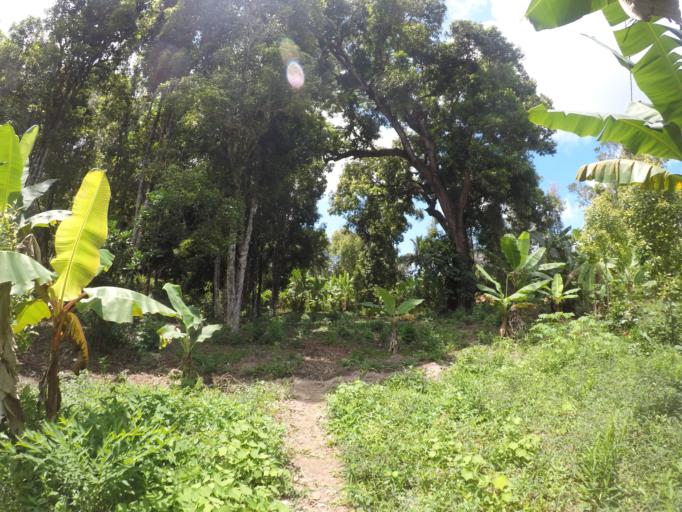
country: TZ
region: Pemba South
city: Mtambile
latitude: -5.3811
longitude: 39.7147
